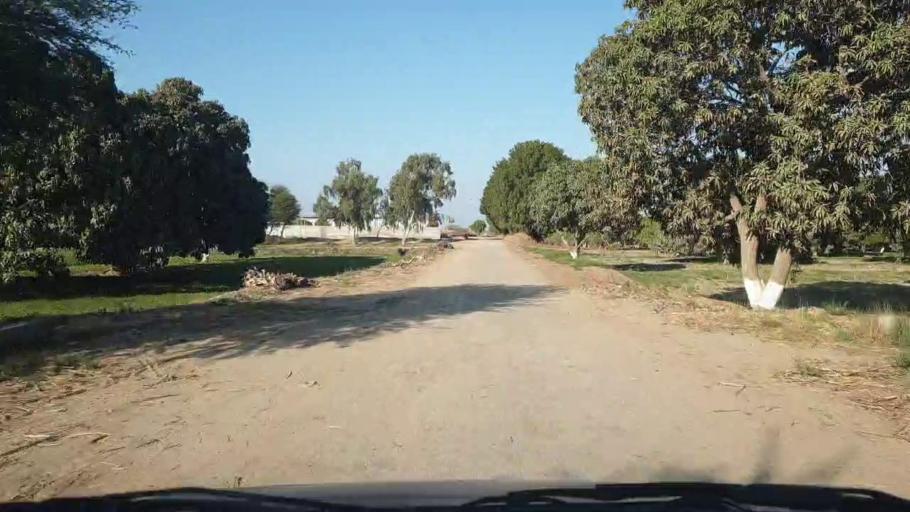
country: PK
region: Sindh
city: Samaro
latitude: 25.3605
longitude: 69.3017
